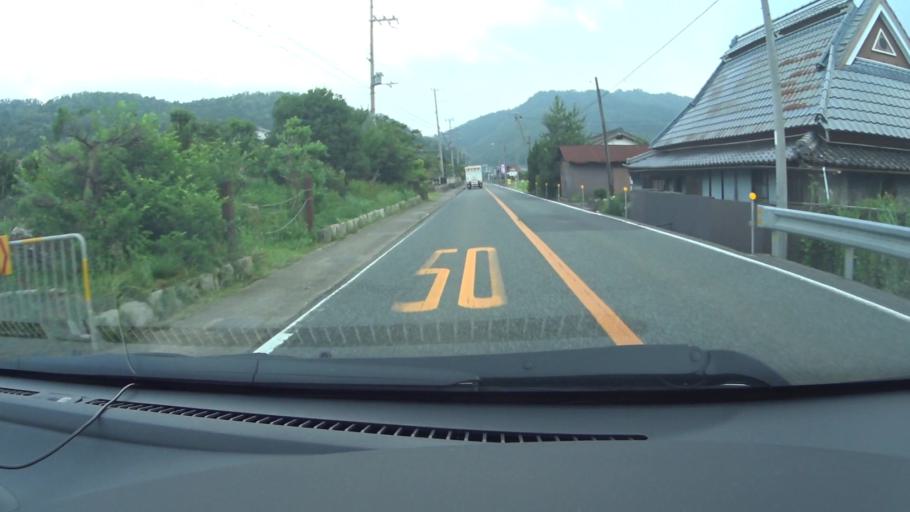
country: JP
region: Kyoto
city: Ayabe
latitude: 35.3574
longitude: 135.3147
